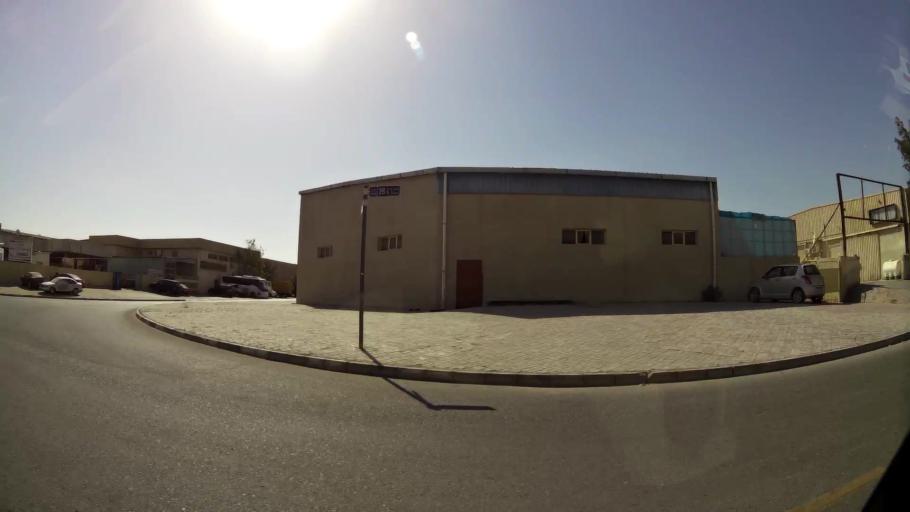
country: AE
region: Dubai
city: Dubai
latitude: 25.1173
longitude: 55.2199
